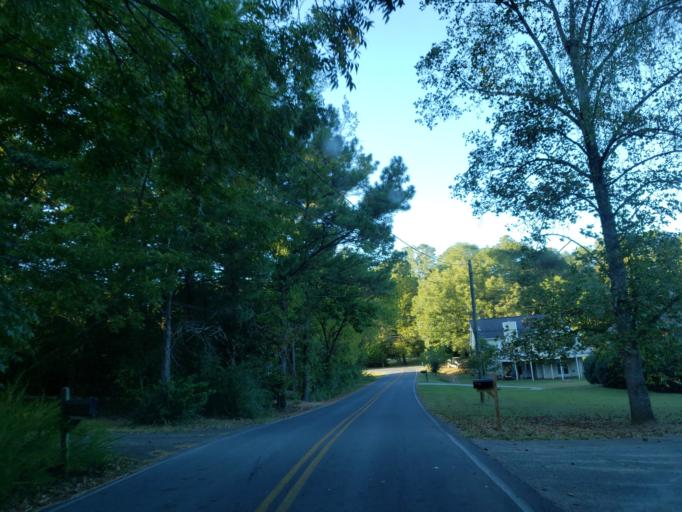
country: US
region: Georgia
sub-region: Pickens County
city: Jasper
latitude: 34.4628
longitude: -84.4272
